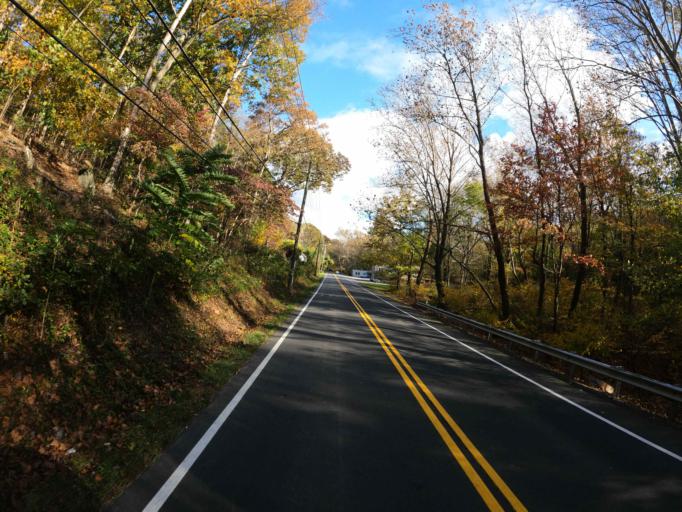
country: US
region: Maryland
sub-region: Carroll County
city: Mount Airy
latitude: 39.3678
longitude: -77.1877
